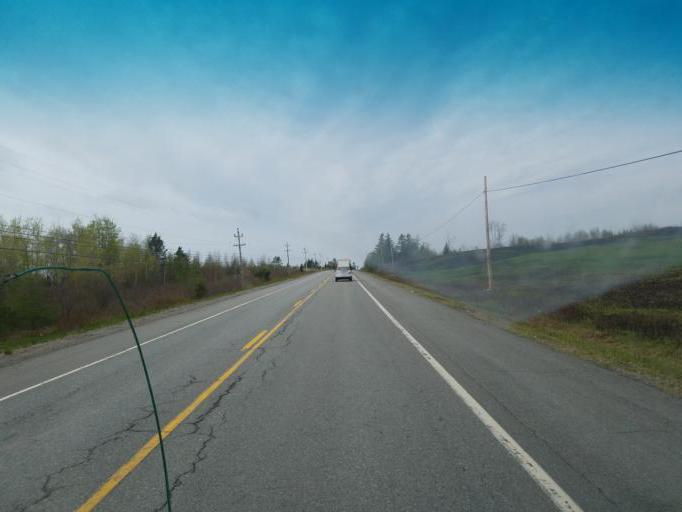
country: US
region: Maine
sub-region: Washington County
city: East Machias
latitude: 44.7561
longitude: -67.2323
